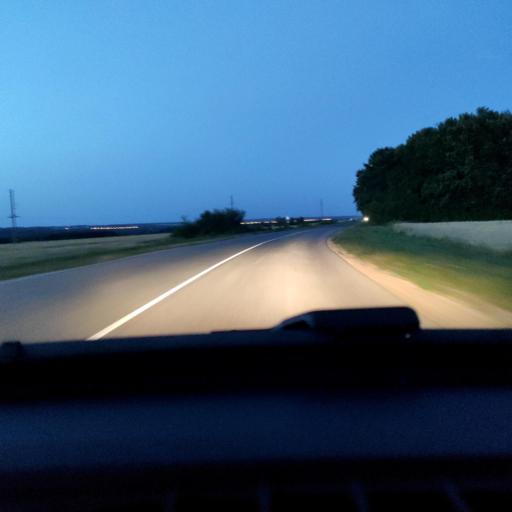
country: RU
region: Lipetsk
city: Zadonsk
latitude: 52.3097
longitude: 38.8838
